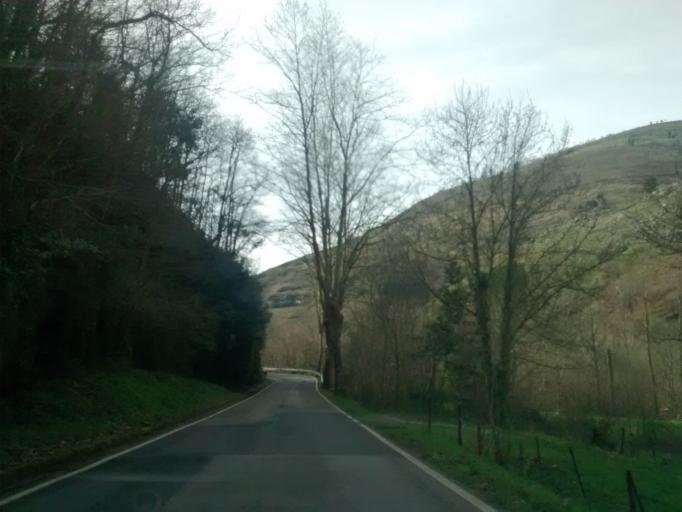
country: ES
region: Cantabria
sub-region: Provincia de Cantabria
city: Vega de Pas
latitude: 43.1684
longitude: -3.8366
